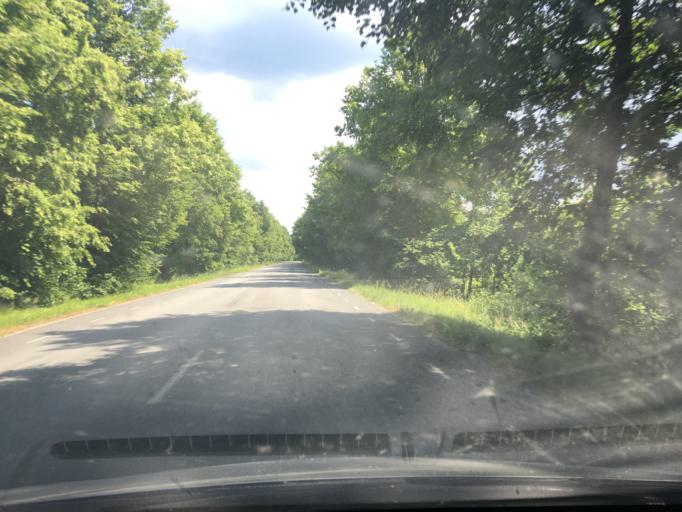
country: EE
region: Paernumaa
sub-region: Halinga vald
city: Parnu-Jaagupi
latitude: 58.7113
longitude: 24.3777
